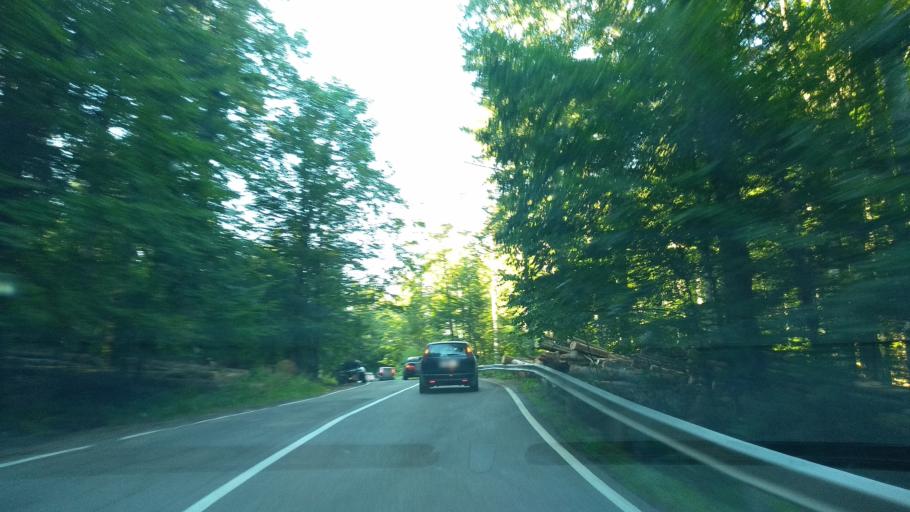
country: RO
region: Prahova
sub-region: Oras Sinaia
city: Sinaia
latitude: 45.3184
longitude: 25.5200
